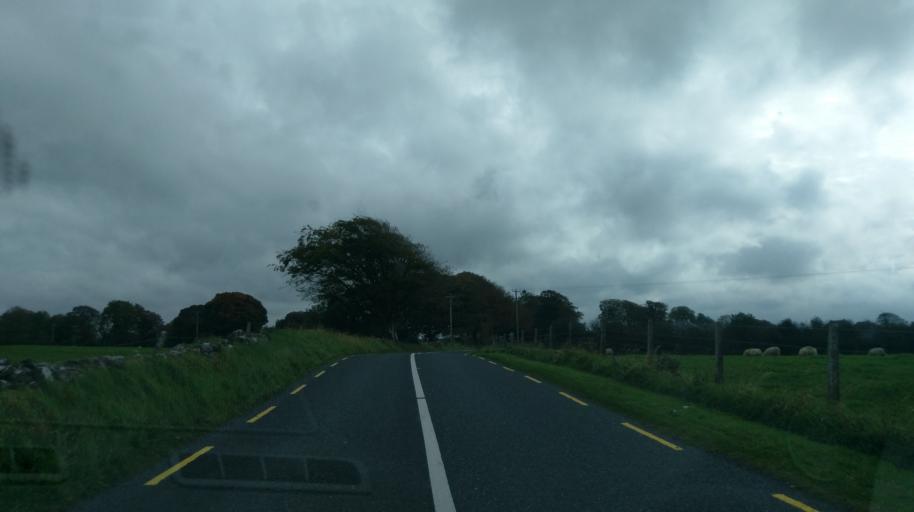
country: IE
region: Connaught
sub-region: County Galway
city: Ballinasloe
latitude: 53.4359
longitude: -8.4493
